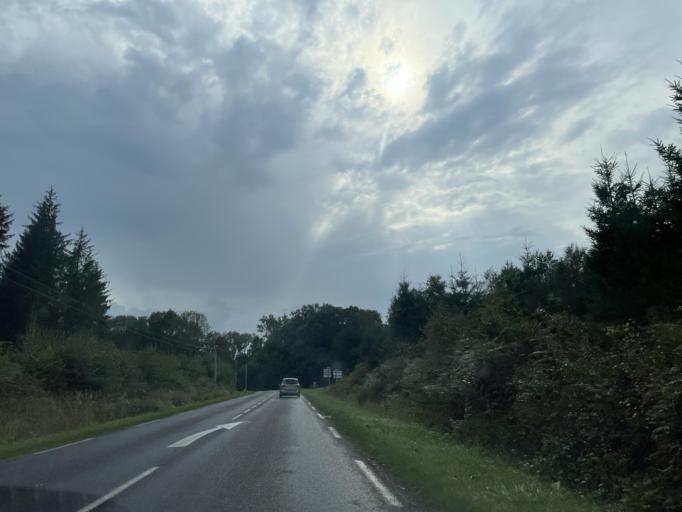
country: FR
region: Haute-Normandie
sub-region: Departement de la Seine-Maritime
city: Neufchatel-en-Bray
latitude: 49.7641
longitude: 1.4270
